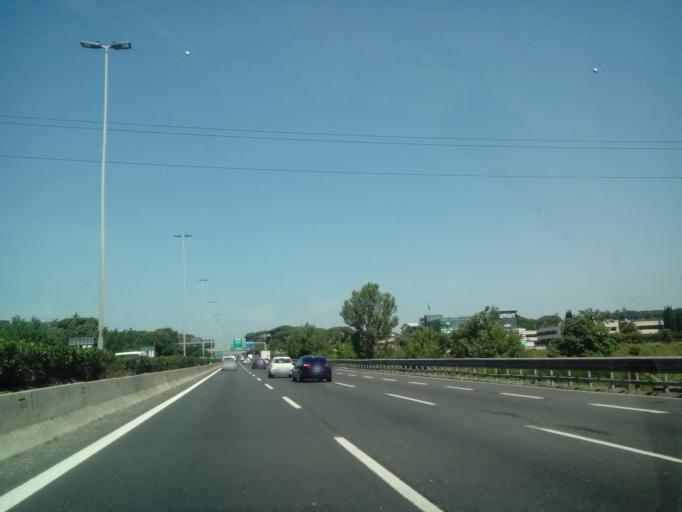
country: IT
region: Latium
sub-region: Citta metropolitana di Roma Capitale
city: Setteville
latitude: 41.9255
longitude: 12.6075
